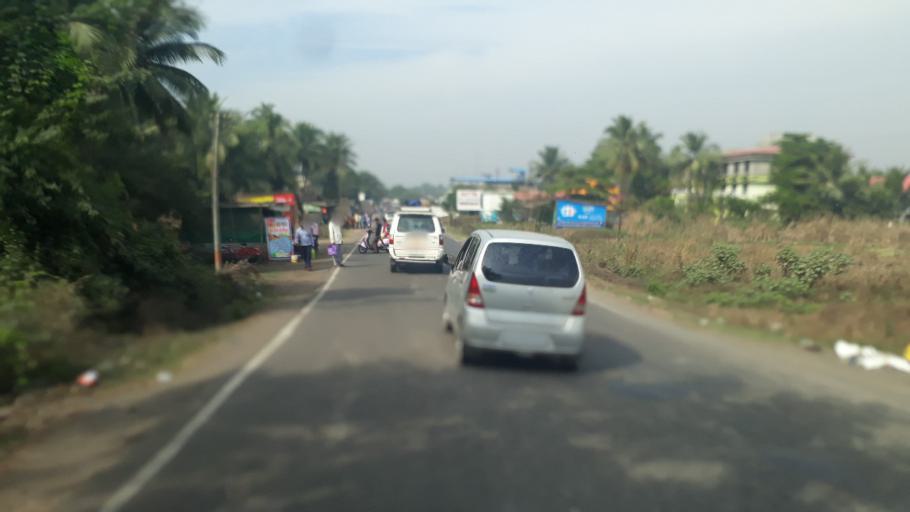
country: IN
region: Maharashtra
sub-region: Raigarh
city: Pen
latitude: 18.6866
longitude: 73.0003
